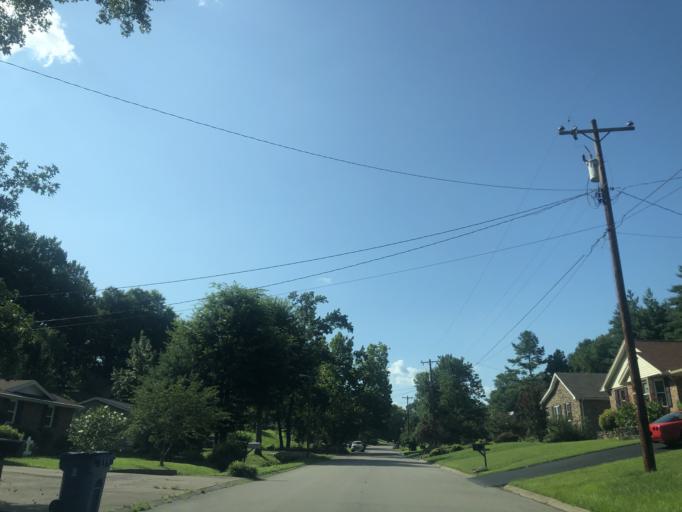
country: US
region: Tennessee
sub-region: Wilson County
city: Green Hill
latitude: 36.2071
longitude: -86.5957
